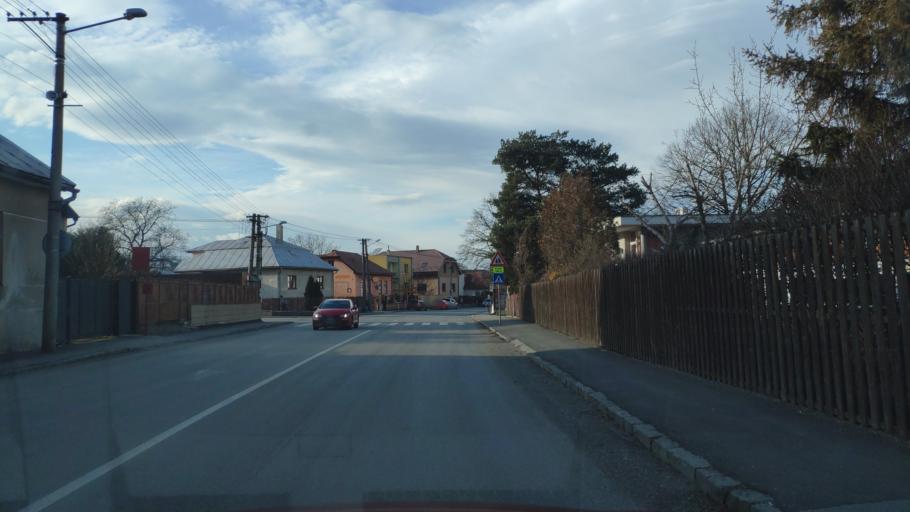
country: SK
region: Kosicky
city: Kosice
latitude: 48.6788
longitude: 21.2637
